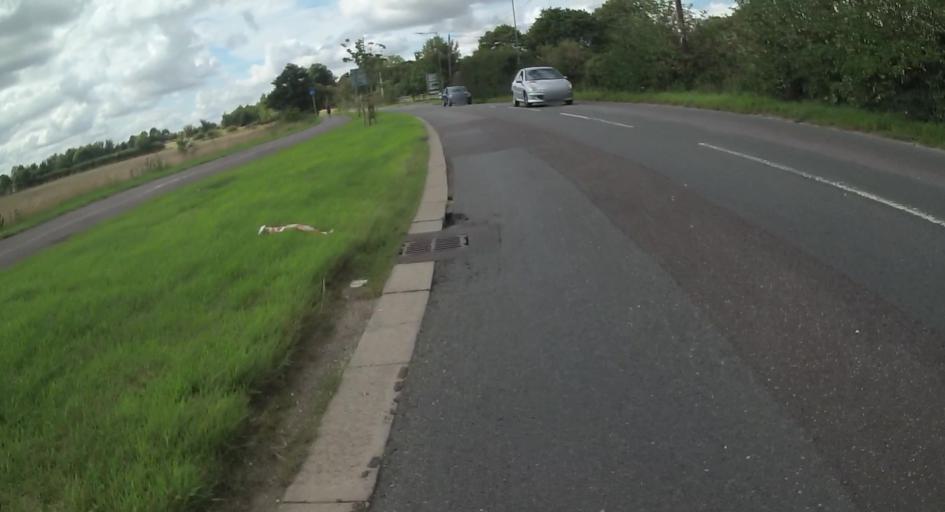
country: GB
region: England
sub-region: West Berkshire
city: Thatcham
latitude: 51.4066
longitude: -1.2855
